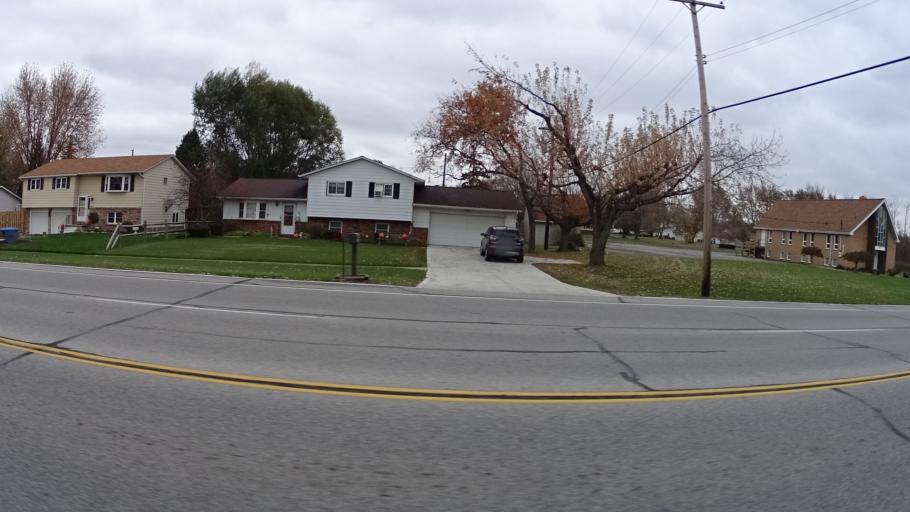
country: US
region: Ohio
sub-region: Lorain County
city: Lorain
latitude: 41.4350
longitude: -82.2025
